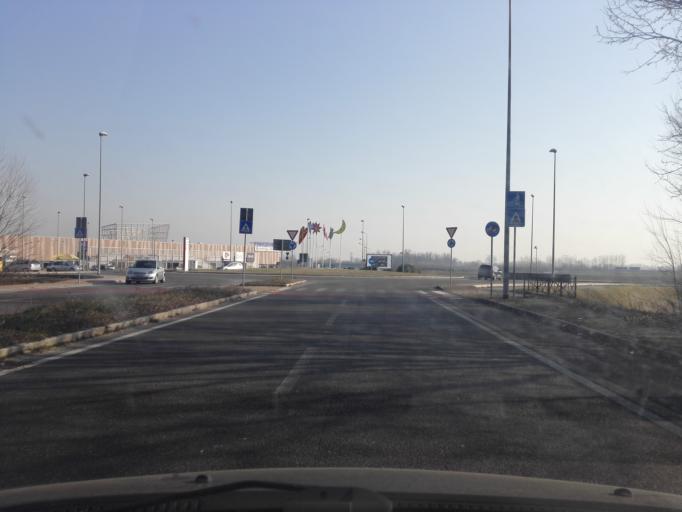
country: IT
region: Piedmont
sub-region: Provincia di Alessandria
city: Alessandria
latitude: 44.9017
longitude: 8.6285
